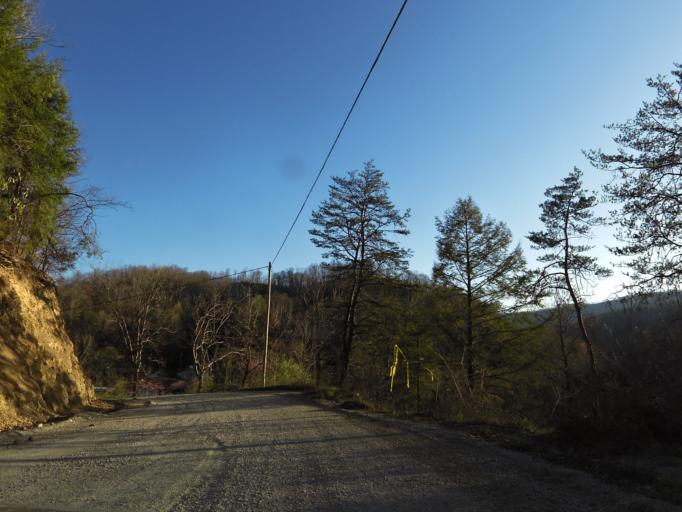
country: US
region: Tennessee
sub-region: Campbell County
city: Caryville
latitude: 36.2394
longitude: -84.3308
